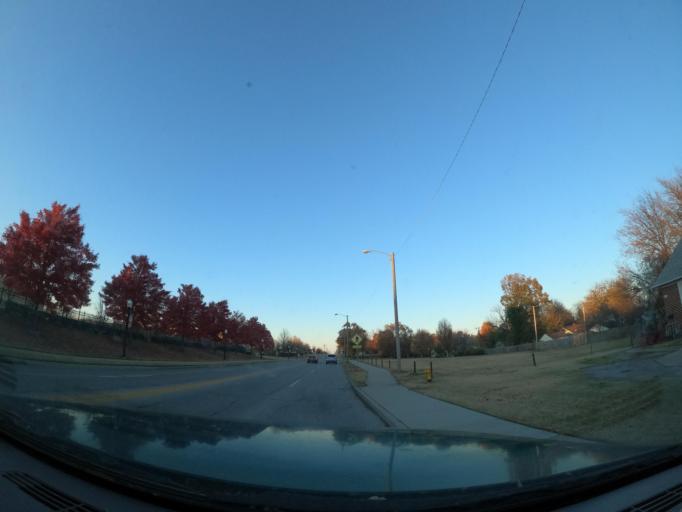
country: US
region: Oklahoma
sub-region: Tulsa County
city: Tulsa
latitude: 36.1489
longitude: -95.9403
